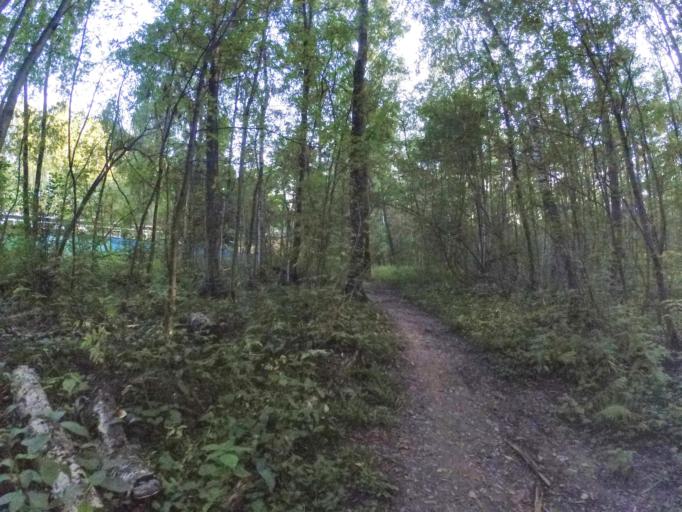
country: RU
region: Moscow
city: Khimki
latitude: 55.8736
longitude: 37.4332
